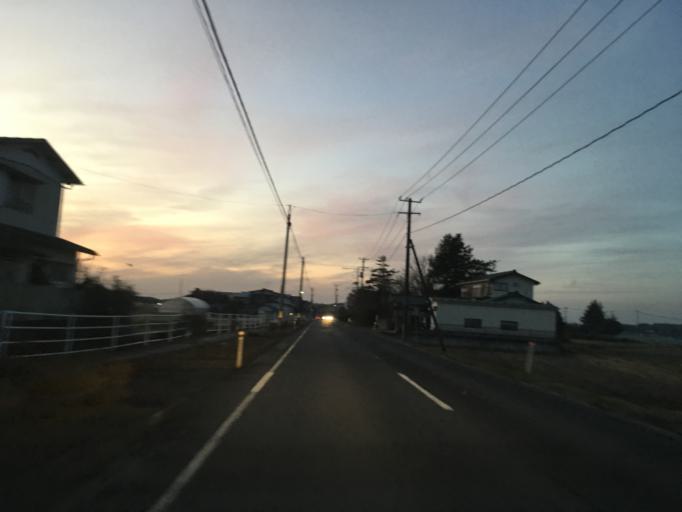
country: JP
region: Miyagi
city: Wakuya
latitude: 38.7131
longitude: 141.2232
